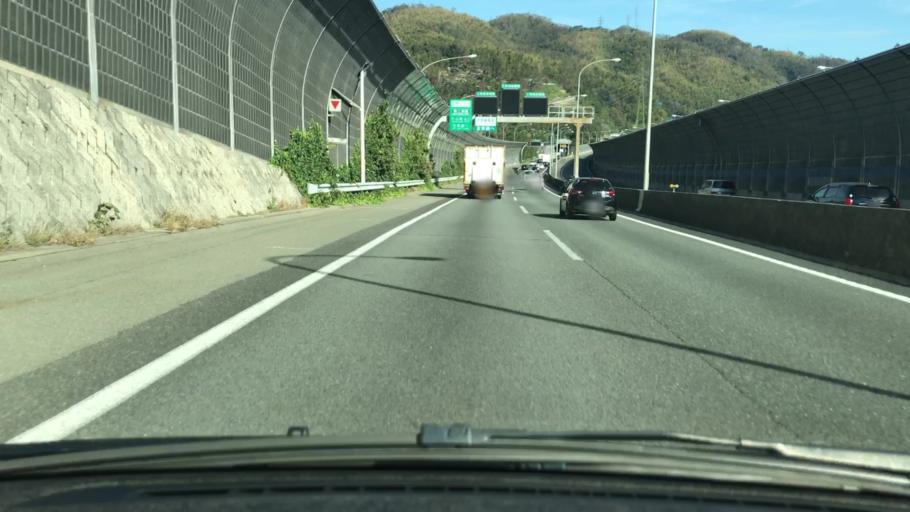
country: JP
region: Kyoto
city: Yawata
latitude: 34.8876
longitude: 135.6621
